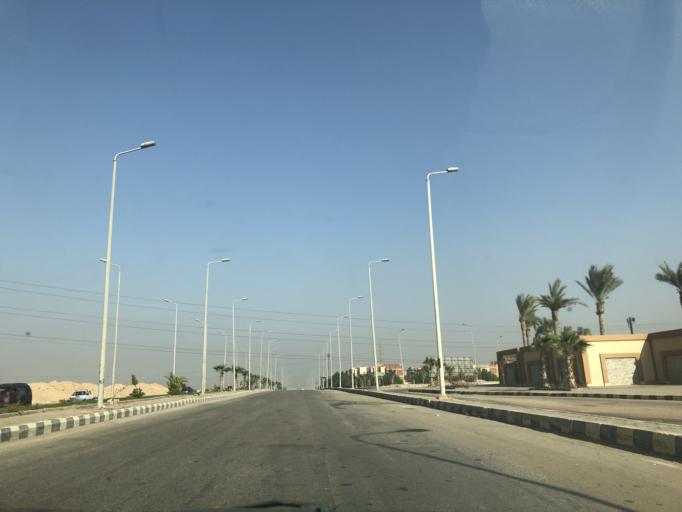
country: EG
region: Al Jizah
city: Madinat Sittah Uktubar
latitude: 29.9458
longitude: 31.0637
